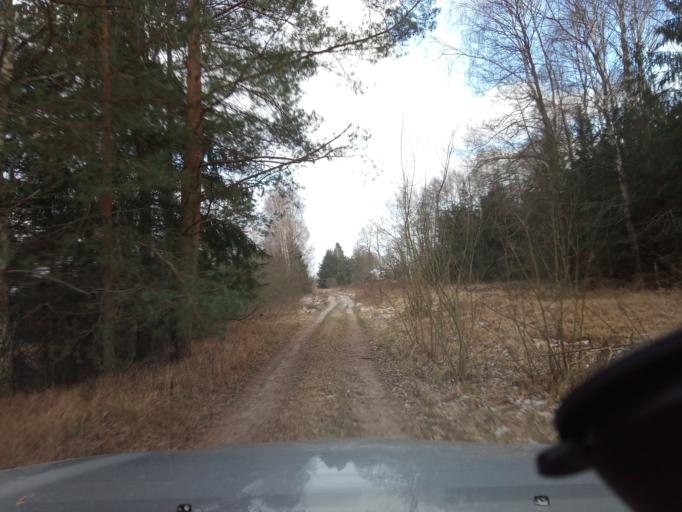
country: LT
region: Alytaus apskritis
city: Druskininkai
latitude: 54.1105
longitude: 24.2272
